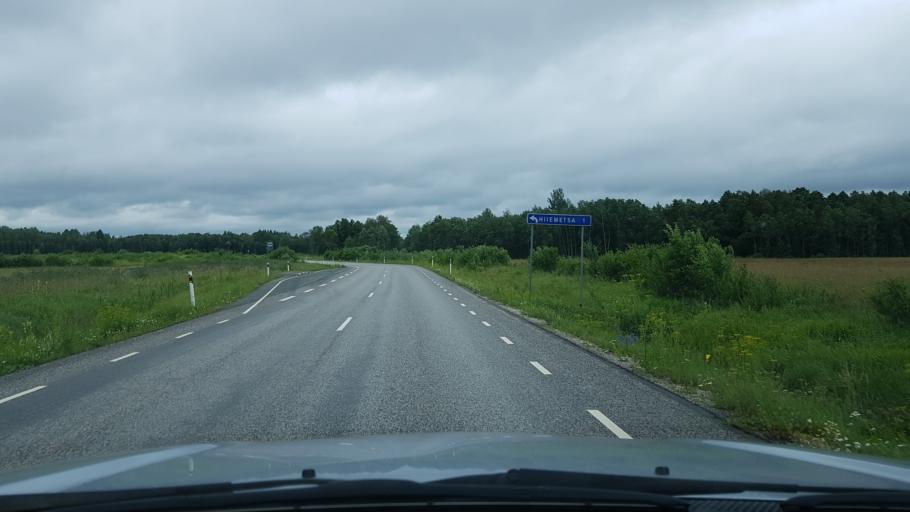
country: EE
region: Ida-Virumaa
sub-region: Narva-Joesuu linn
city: Narva-Joesuu
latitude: 59.3714
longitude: 27.9301
